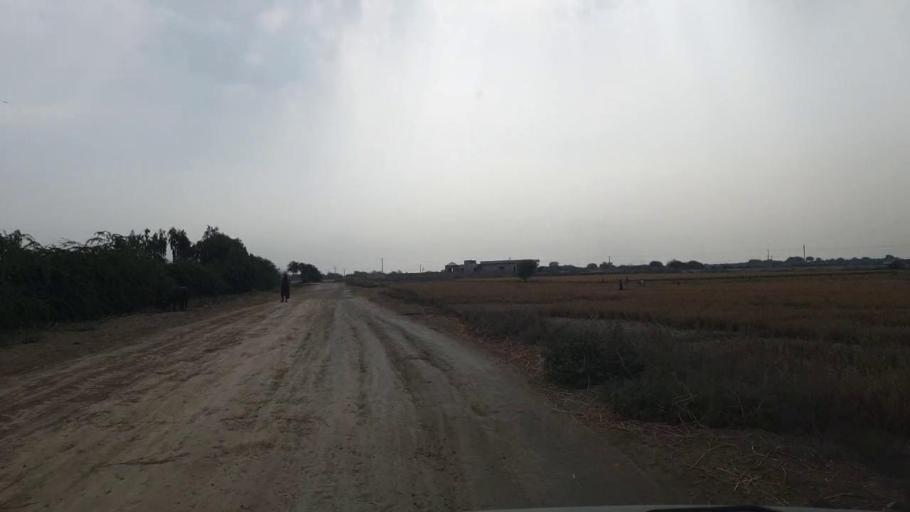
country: PK
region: Sindh
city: Talhar
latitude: 24.9015
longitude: 68.7722
